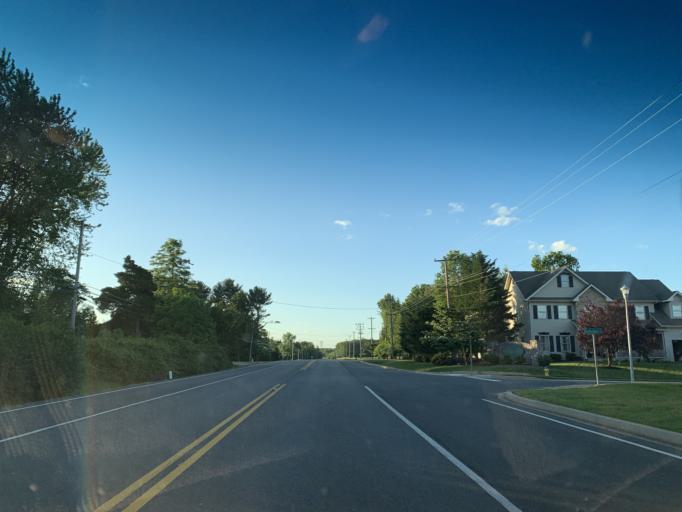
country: US
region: Maryland
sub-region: Cecil County
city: Elkton
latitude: 39.6298
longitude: -75.8415
